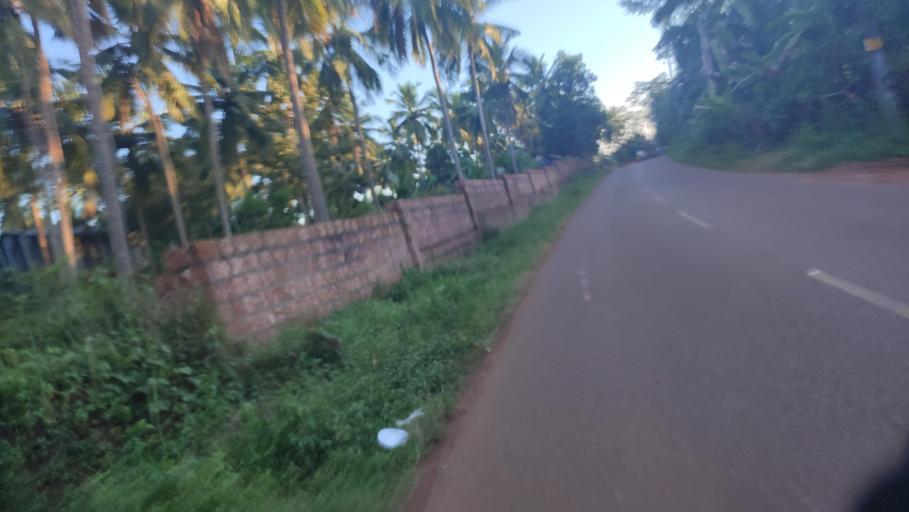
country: IN
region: Kerala
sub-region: Kasaragod District
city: Kannangad
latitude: 12.4009
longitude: 75.0634
